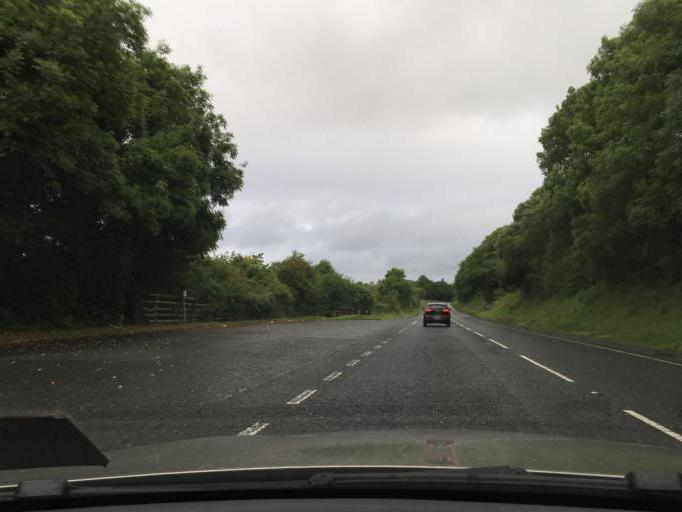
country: GB
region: Northern Ireland
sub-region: Fermanagh District
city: Enniskillen
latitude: 54.3769
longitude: -7.6355
